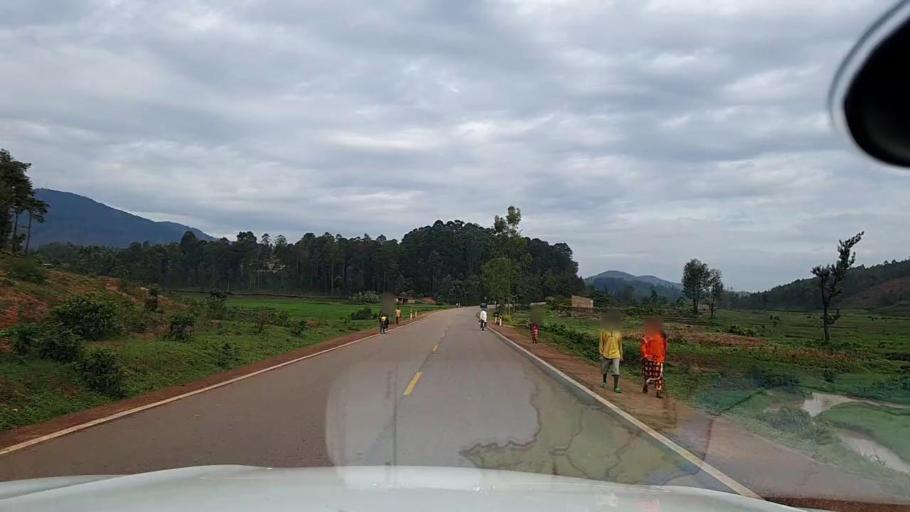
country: RW
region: Southern Province
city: Butare
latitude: -2.5660
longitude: 29.7258
